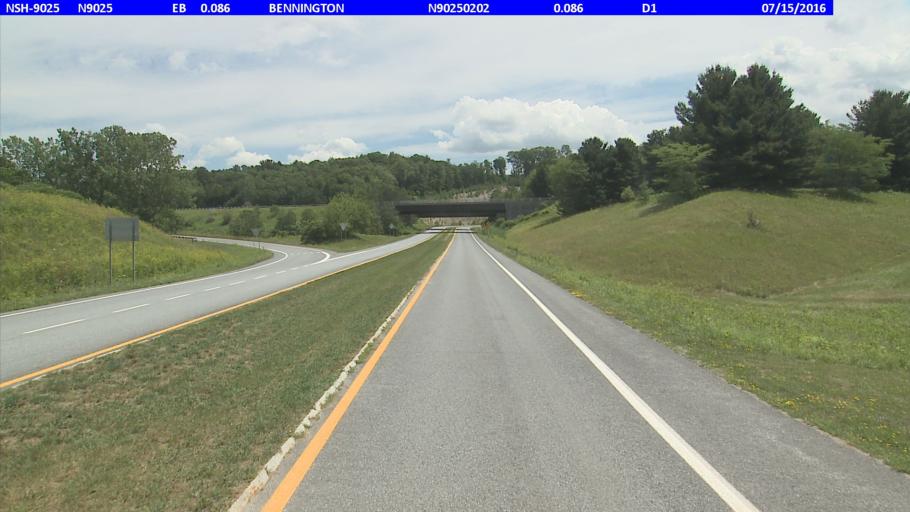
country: US
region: Vermont
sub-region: Bennington County
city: North Bennington
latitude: 42.9234
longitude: -73.2081
